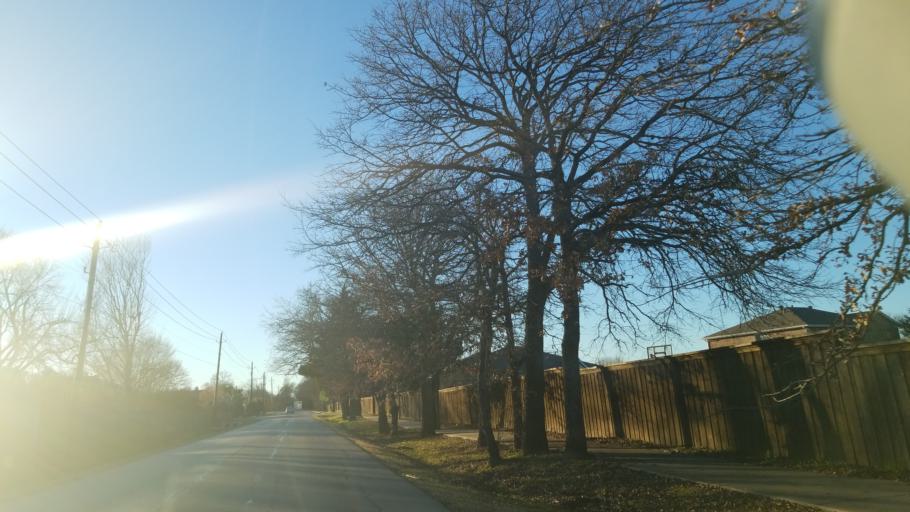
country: US
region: Texas
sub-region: Denton County
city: Hickory Creek
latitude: 33.1446
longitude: -97.0402
